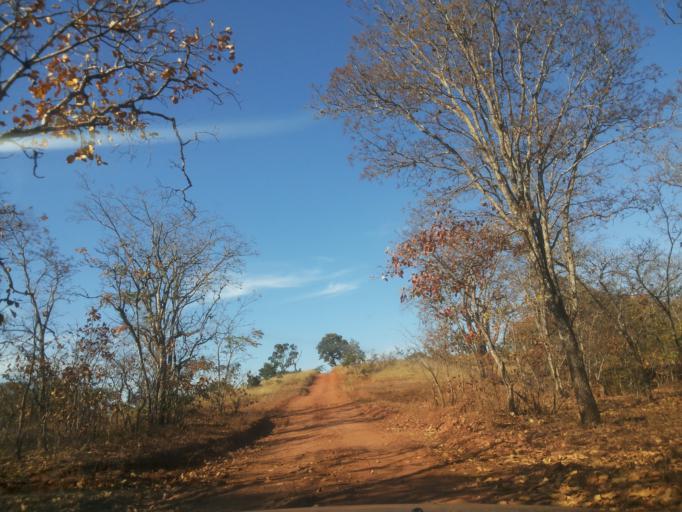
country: BR
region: Minas Gerais
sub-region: Ituiutaba
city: Ituiutaba
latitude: -19.1042
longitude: -49.4173
